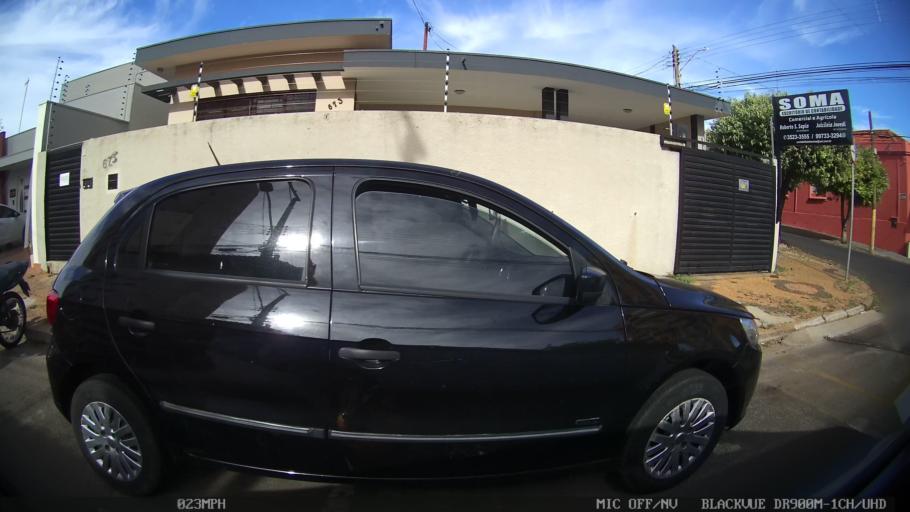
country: BR
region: Sao Paulo
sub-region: Catanduva
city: Catanduva
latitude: -21.1334
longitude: -48.9767
